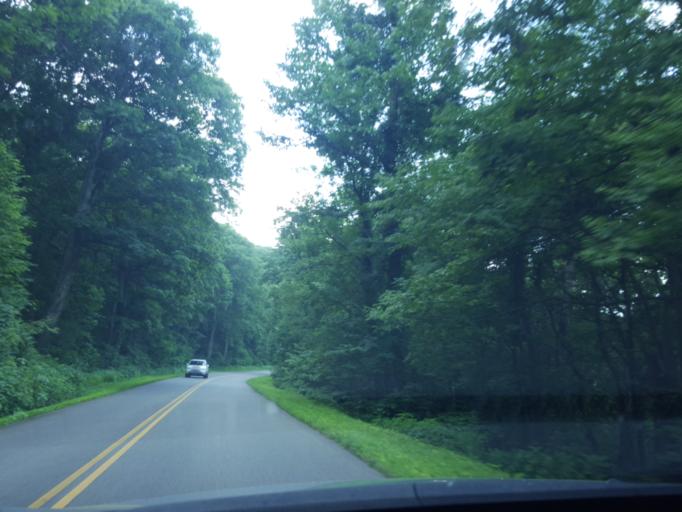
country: US
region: Virginia
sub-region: Nelson County
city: Nellysford
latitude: 37.9503
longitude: -78.9143
